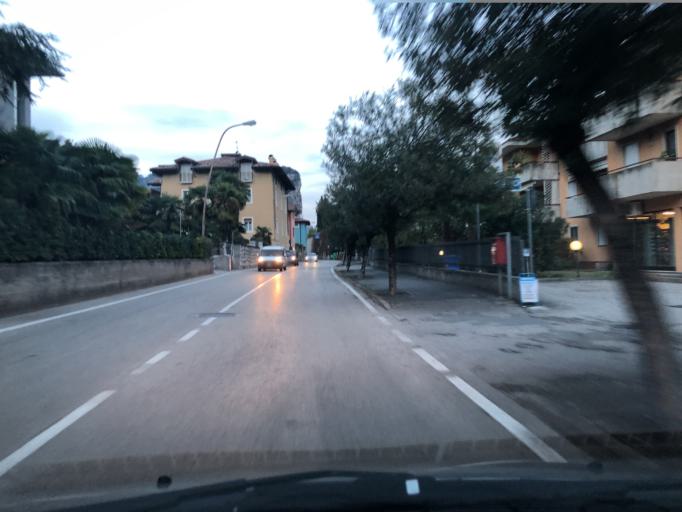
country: IT
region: Trentino-Alto Adige
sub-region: Provincia di Trento
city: Arco
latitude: 45.9130
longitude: 10.8827
